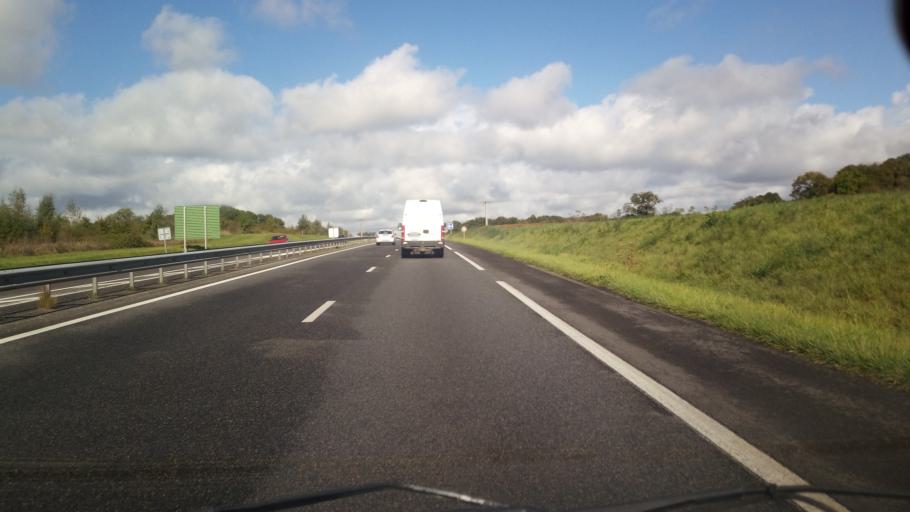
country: FR
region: Centre
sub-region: Departement du Loiret
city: Gien
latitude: 47.7003
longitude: 2.6461
